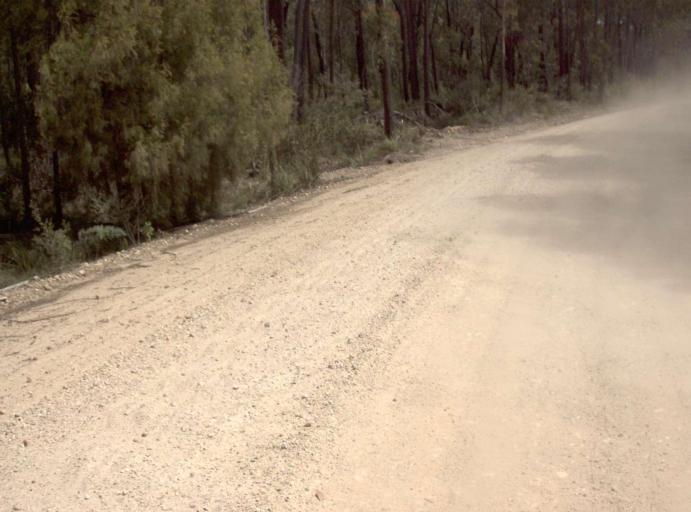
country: AU
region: Victoria
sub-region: East Gippsland
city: Lakes Entrance
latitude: -37.6725
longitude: 148.6326
